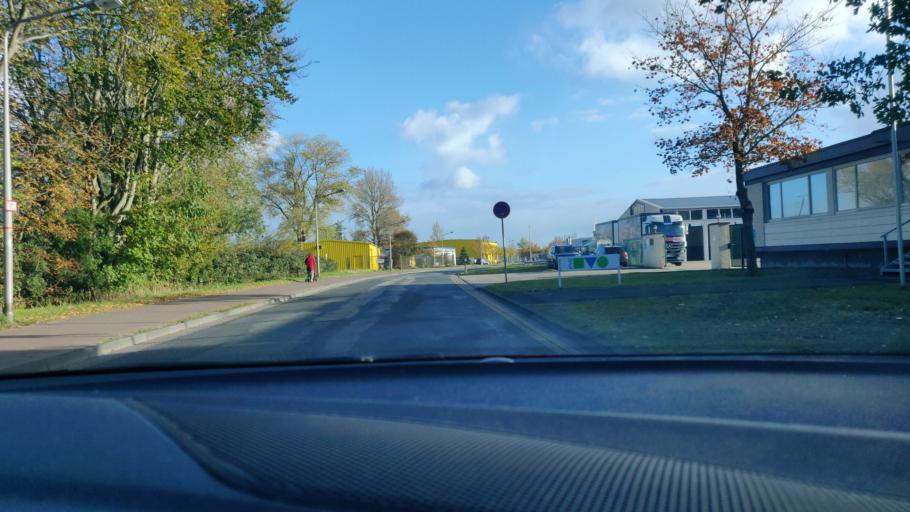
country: DE
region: Lower Saxony
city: Cuxhaven
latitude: 53.8573
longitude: 8.7093
